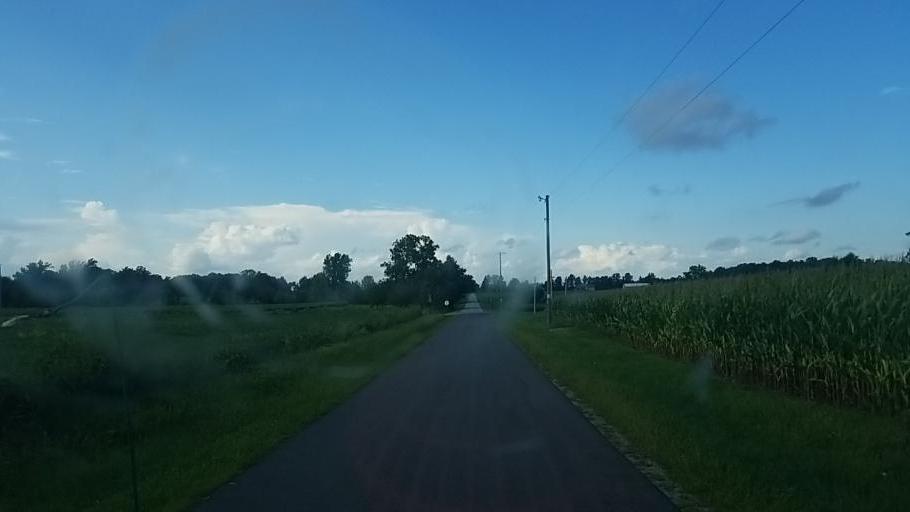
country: US
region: Ohio
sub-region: Hardin County
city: Forest
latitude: 40.7879
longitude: -83.4484
